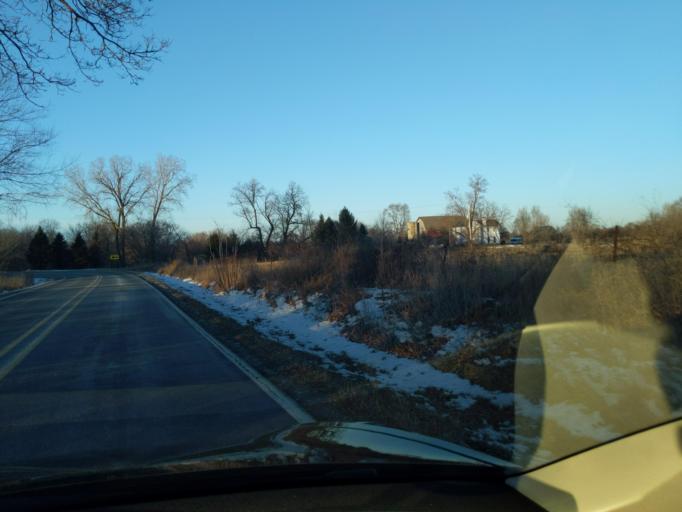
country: US
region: Michigan
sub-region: Ingham County
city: Stockbridge
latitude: 42.4909
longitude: -84.2181
